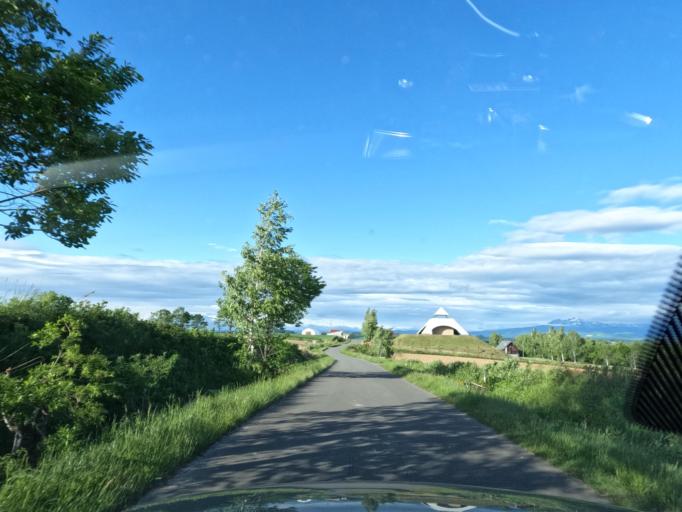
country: JP
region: Hokkaido
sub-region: Asahikawa-shi
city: Asahikawa
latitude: 43.6042
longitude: 142.4545
